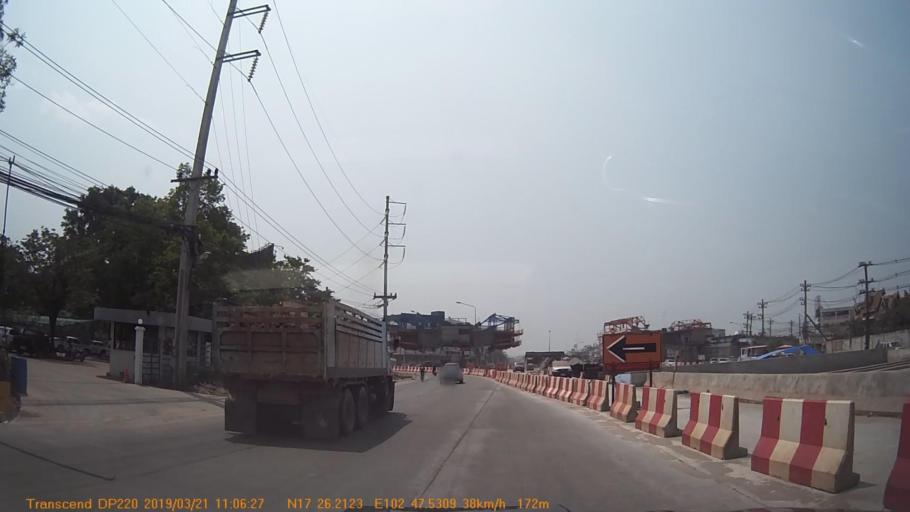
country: TH
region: Changwat Udon Thani
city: Udon Thani
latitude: 17.4367
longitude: 102.7922
